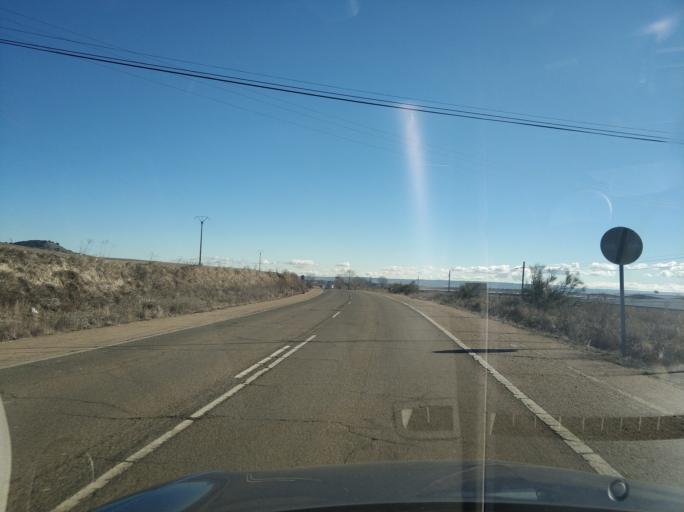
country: ES
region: Castille and Leon
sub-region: Provincia de Valladolid
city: Cisterniga
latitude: 41.6016
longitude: -4.6711
